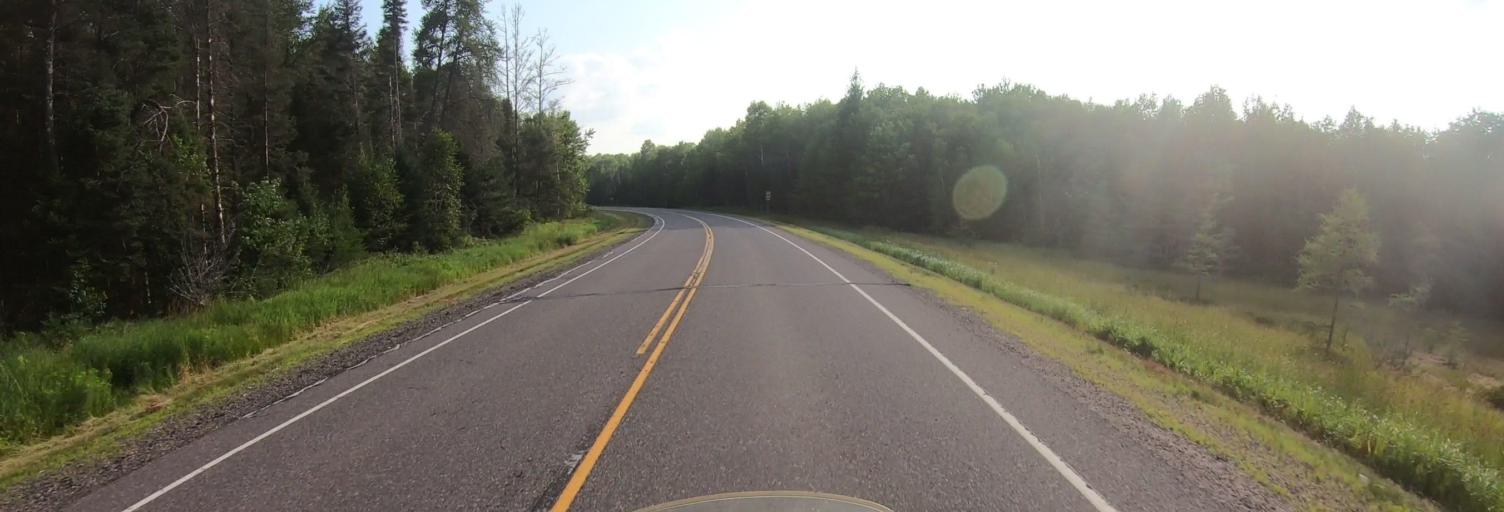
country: US
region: Wisconsin
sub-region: Sawyer County
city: Little Round Lake
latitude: 46.0977
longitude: -91.0025
